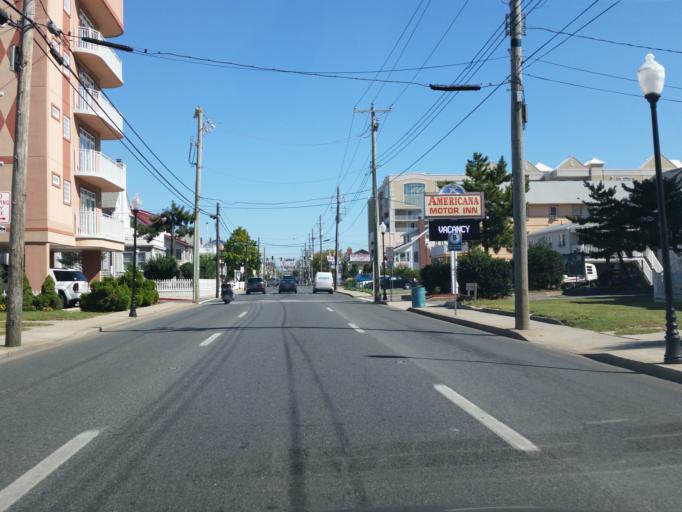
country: US
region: Maryland
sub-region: Worcester County
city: Ocean City
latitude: 38.3368
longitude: -75.0834
